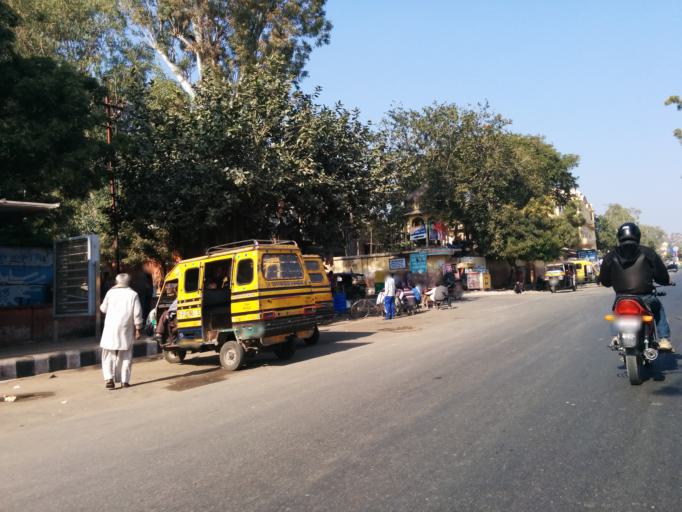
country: IN
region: Rajasthan
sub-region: Jaipur
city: Jaipur
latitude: 26.9520
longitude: 75.8417
